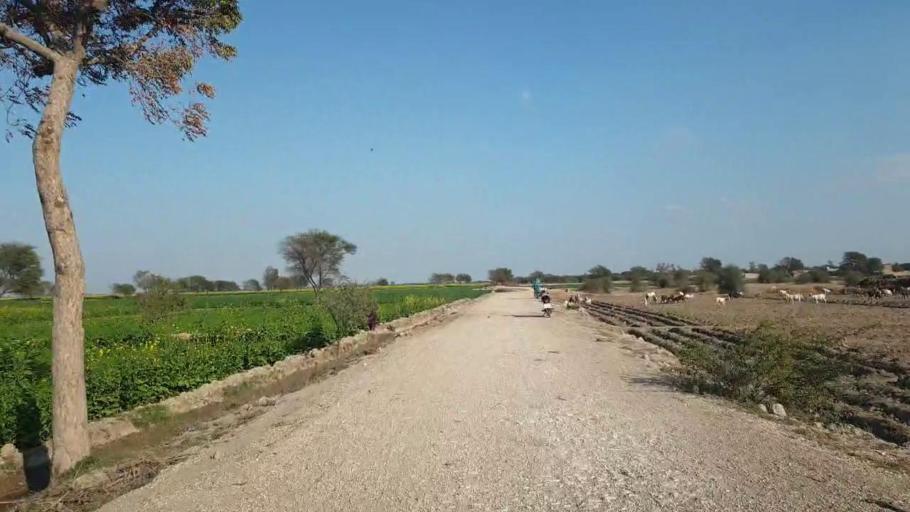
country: PK
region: Sindh
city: Shahpur Chakar
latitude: 26.1197
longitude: 68.5716
